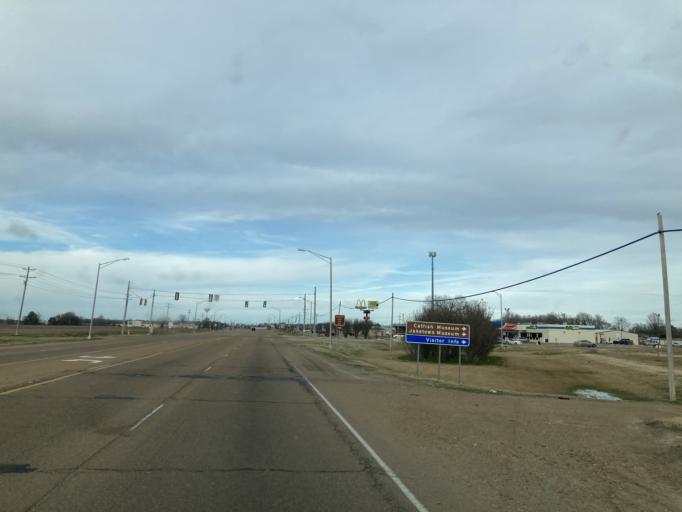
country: US
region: Mississippi
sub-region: Humphreys County
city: Belzoni
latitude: 33.1771
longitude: -90.4974
